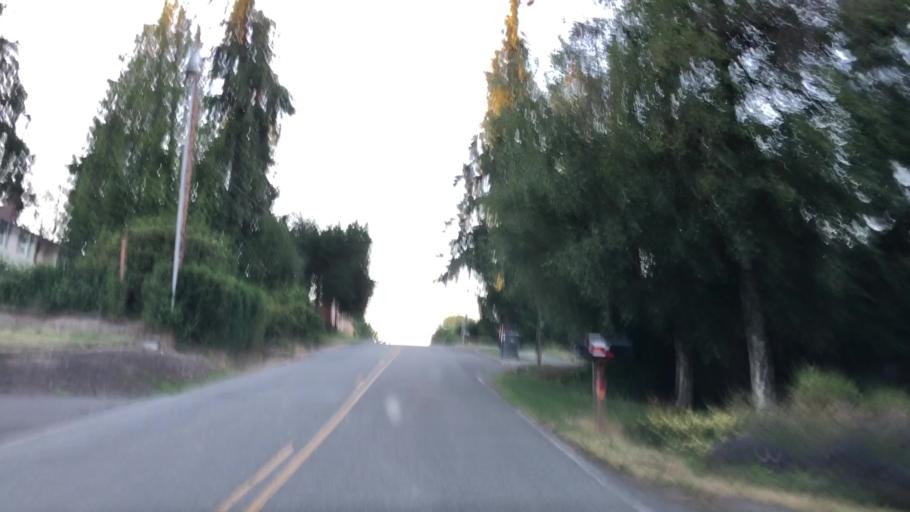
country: US
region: Washington
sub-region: Snohomish County
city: Brier
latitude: 47.7829
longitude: -122.2719
